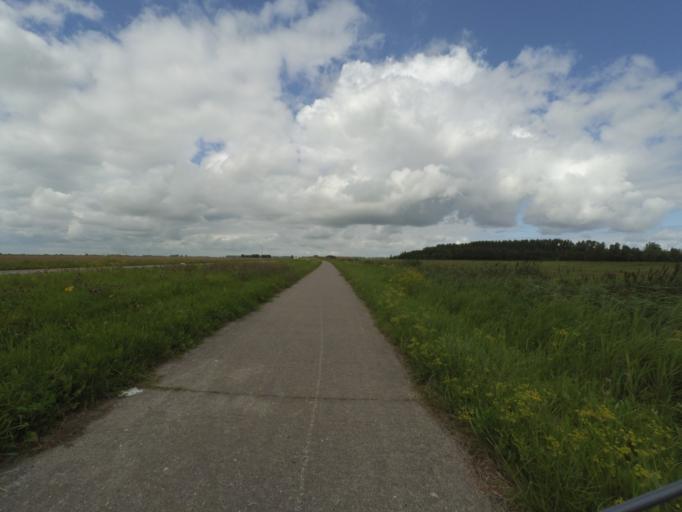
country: NL
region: Groningen
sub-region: Gemeente Zuidhorn
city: Grijpskerk
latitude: 53.3205
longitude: 6.2448
